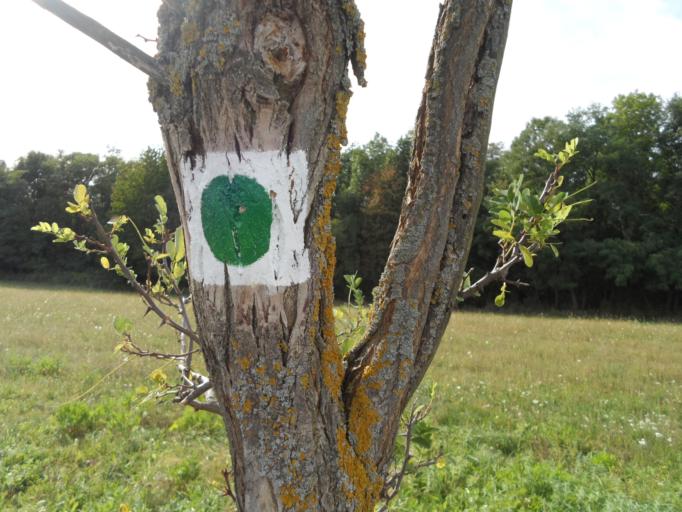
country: HU
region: Veszprem
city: Ajka
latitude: 47.1945
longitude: 17.6118
